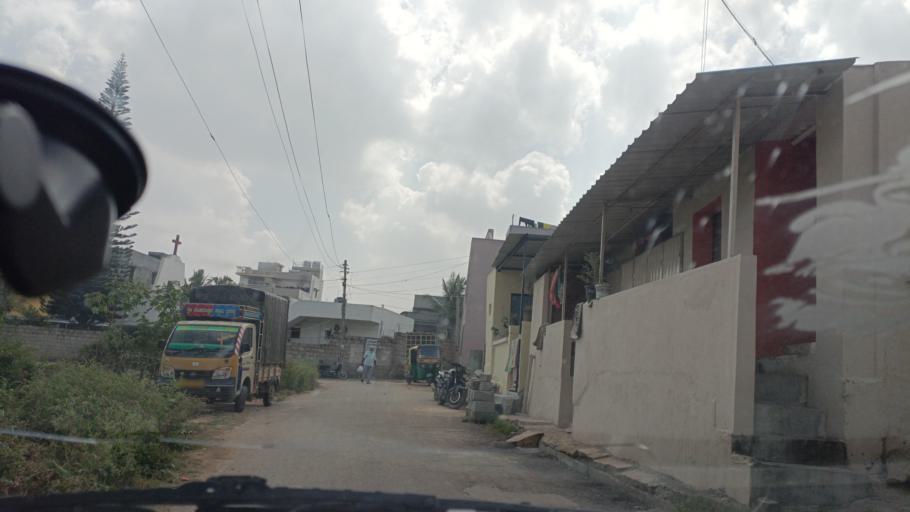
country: IN
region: Karnataka
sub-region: Bangalore Urban
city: Yelahanka
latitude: 13.1654
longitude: 77.6354
